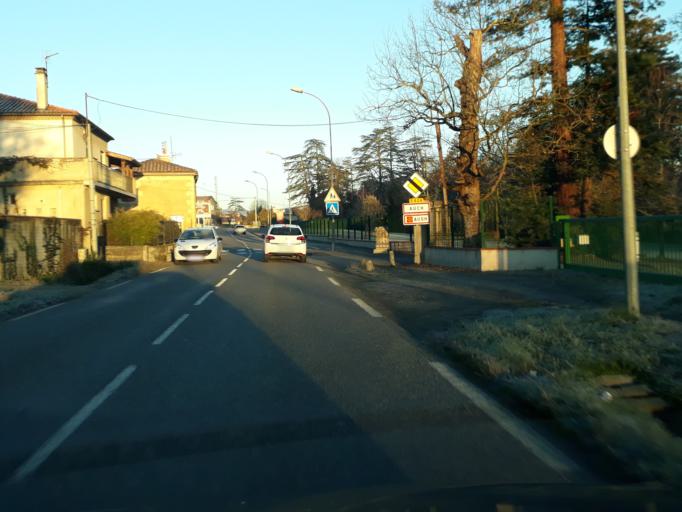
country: FR
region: Midi-Pyrenees
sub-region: Departement du Gers
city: Auch
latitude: 43.6384
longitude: 0.6012
